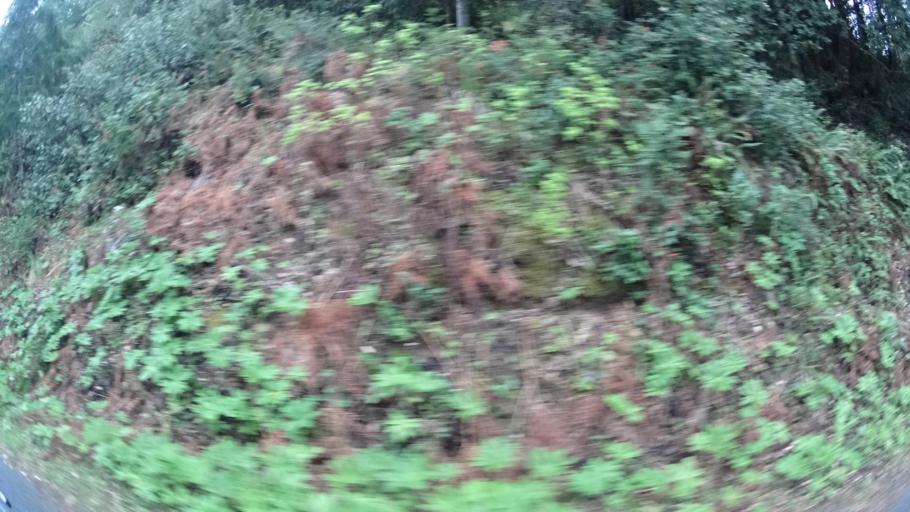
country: US
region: California
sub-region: Humboldt County
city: Redway
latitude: 40.2728
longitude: -123.7742
